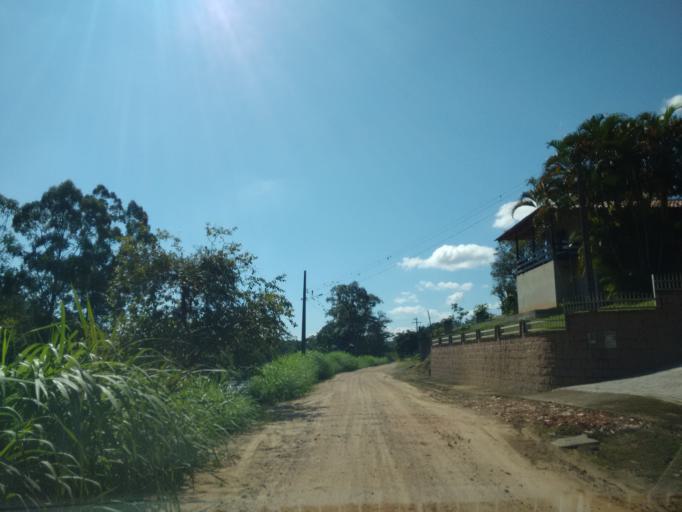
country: BR
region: Santa Catarina
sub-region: Indaial
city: Indaial
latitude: -26.9183
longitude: -49.1904
